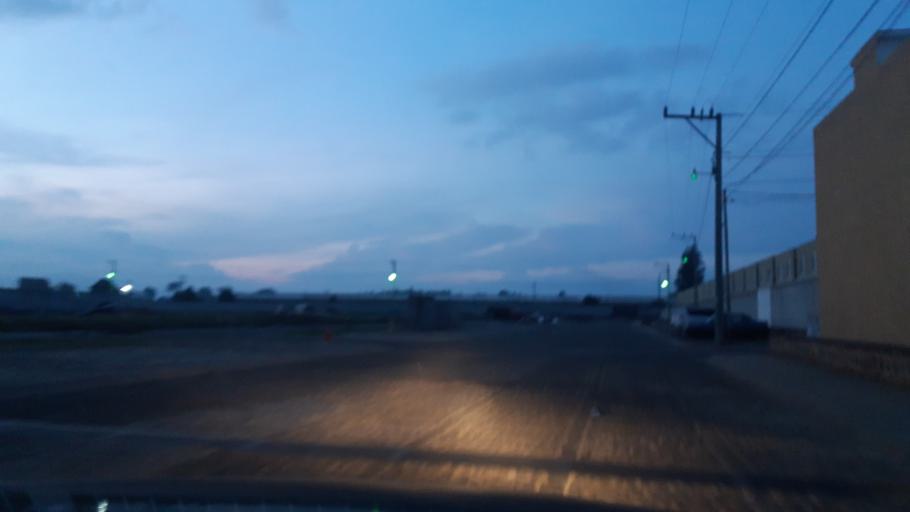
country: GT
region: Chimaltenango
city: El Tejar
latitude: 14.6557
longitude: -90.7995
